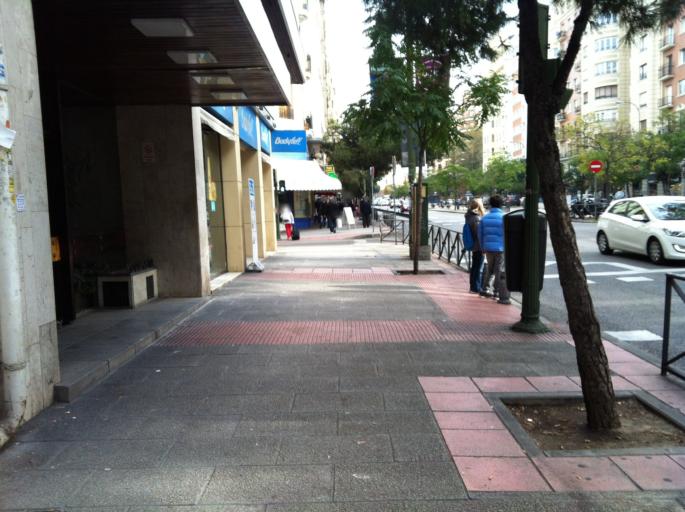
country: ES
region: Madrid
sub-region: Provincia de Madrid
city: Chamberi
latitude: 40.4465
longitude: -3.7127
